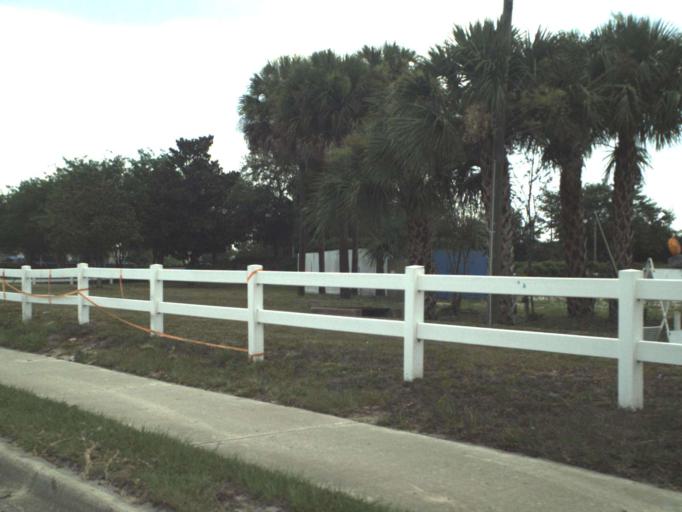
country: US
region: Florida
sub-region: Orange County
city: Fairview Shores
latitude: 28.6004
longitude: -81.4123
